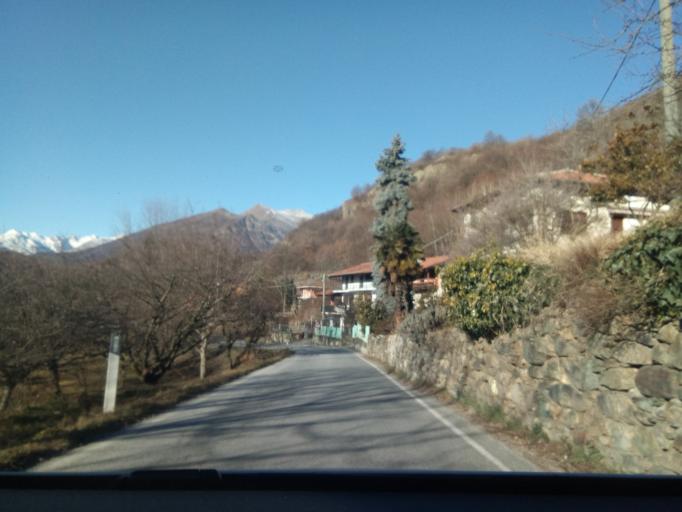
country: IT
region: Piedmont
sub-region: Provincia di Torino
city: Chiaverano
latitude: 45.5122
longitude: 7.8931
